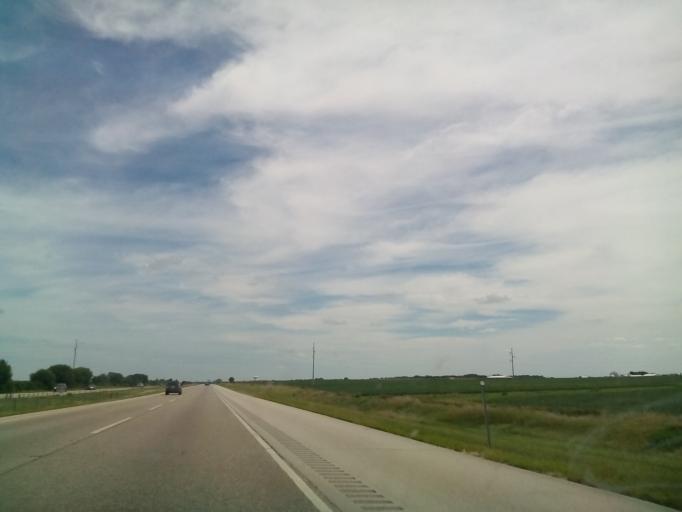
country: US
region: Illinois
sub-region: DeKalb County
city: Malta
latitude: 41.9000
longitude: -88.8157
